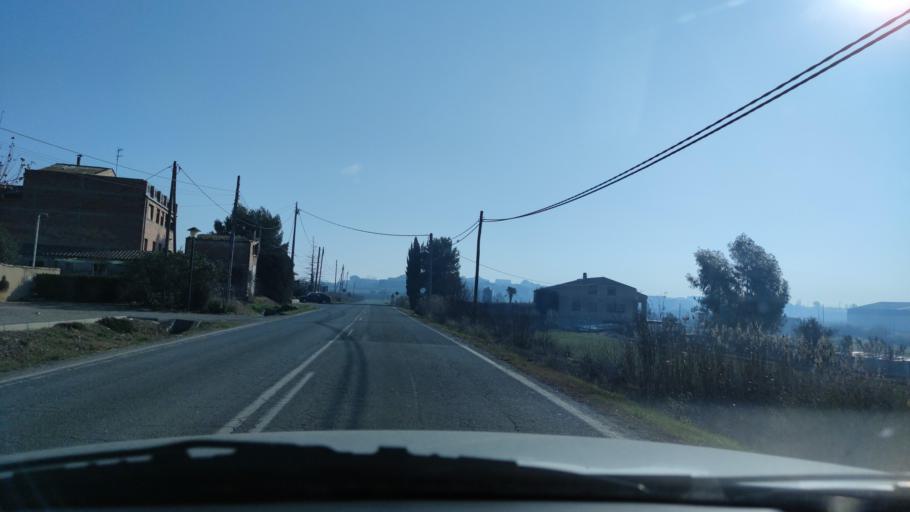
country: ES
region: Catalonia
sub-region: Provincia de Lleida
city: Alcoletge
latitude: 41.6204
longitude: 0.7308
